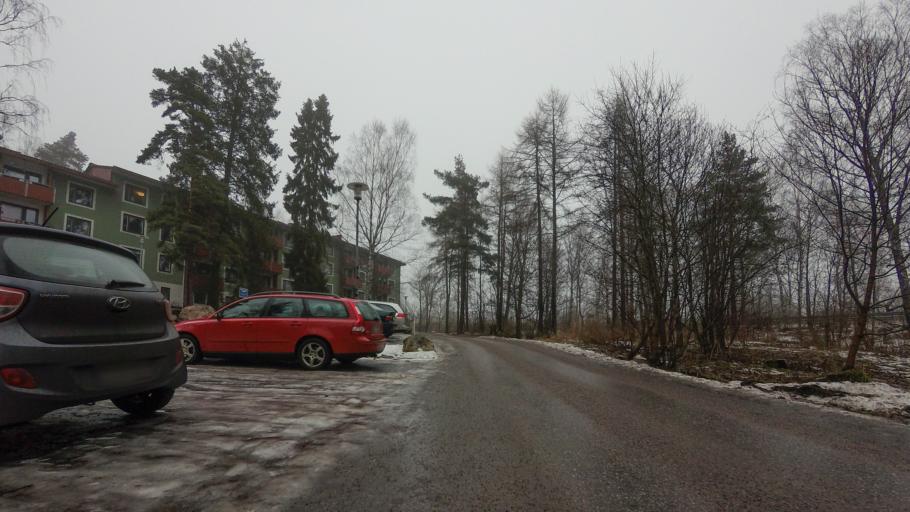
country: FI
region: Uusimaa
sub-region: Helsinki
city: Vantaa
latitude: 60.2076
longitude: 25.0467
